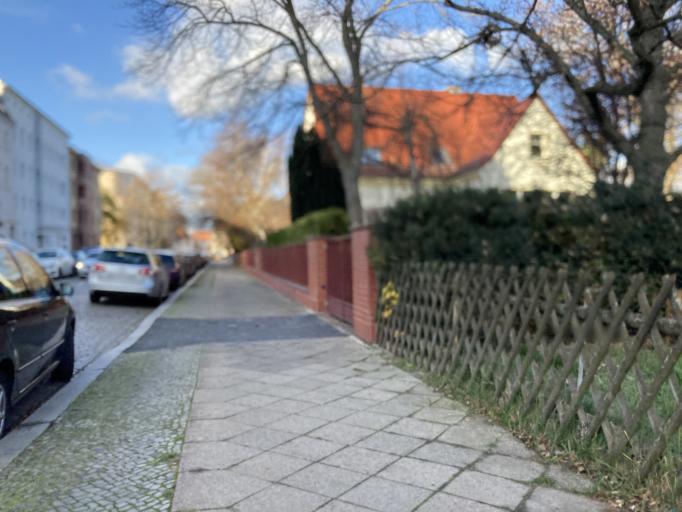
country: DE
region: Saxony-Anhalt
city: Magdeburg
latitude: 52.1356
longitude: 11.6212
